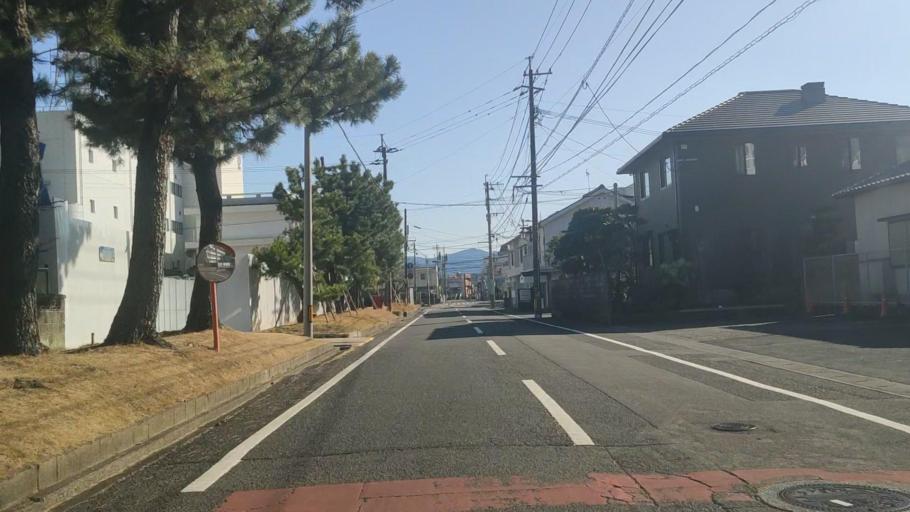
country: JP
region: Oita
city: Saiki
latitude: 32.9608
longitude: 131.8959
